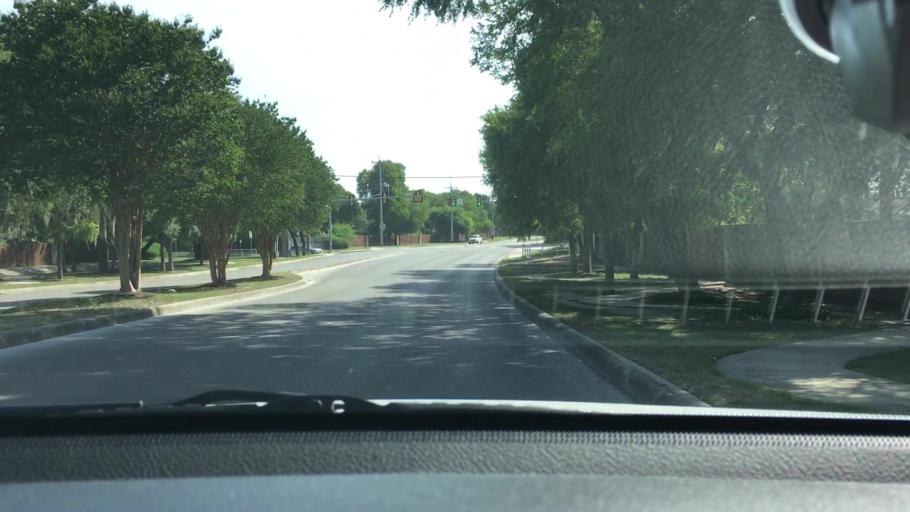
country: US
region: Texas
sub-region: Bexar County
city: Live Oak
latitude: 29.5943
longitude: -98.3906
